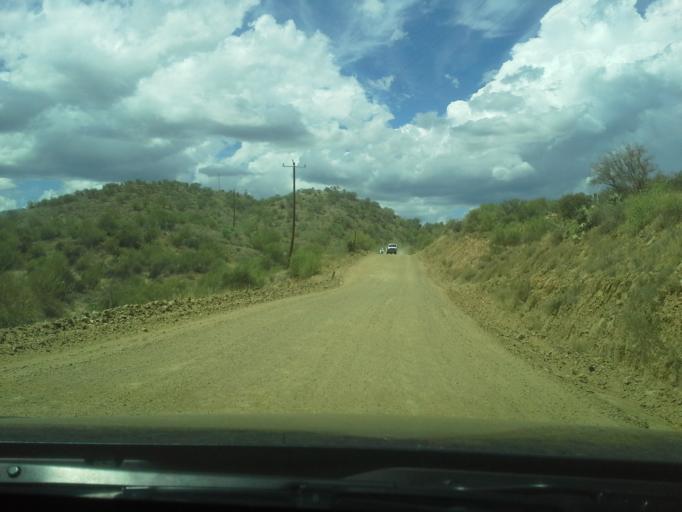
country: US
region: Arizona
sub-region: Yavapai County
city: Spring Valley
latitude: 34.2735
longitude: -112.2138
